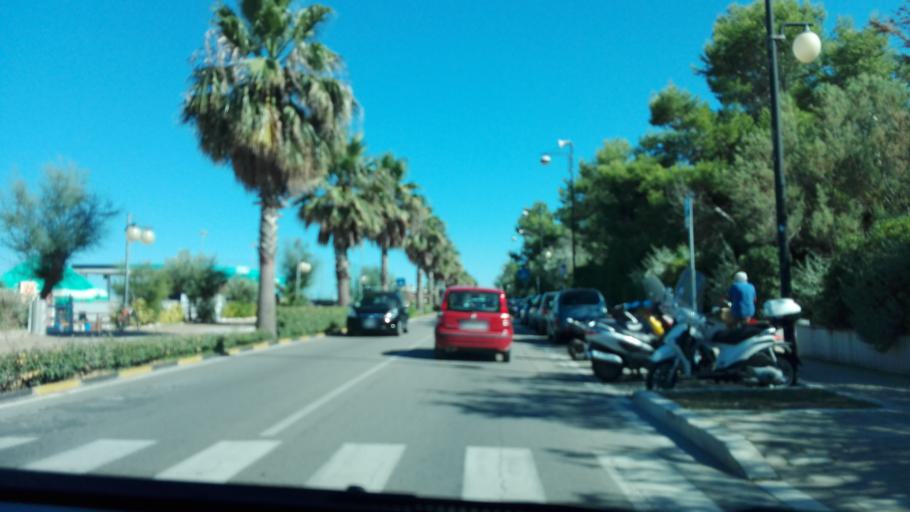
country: IT
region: Abruzzo
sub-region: Provincia di Pescara
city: Montesilvano Marina
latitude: 42.5053
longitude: 14.1734
